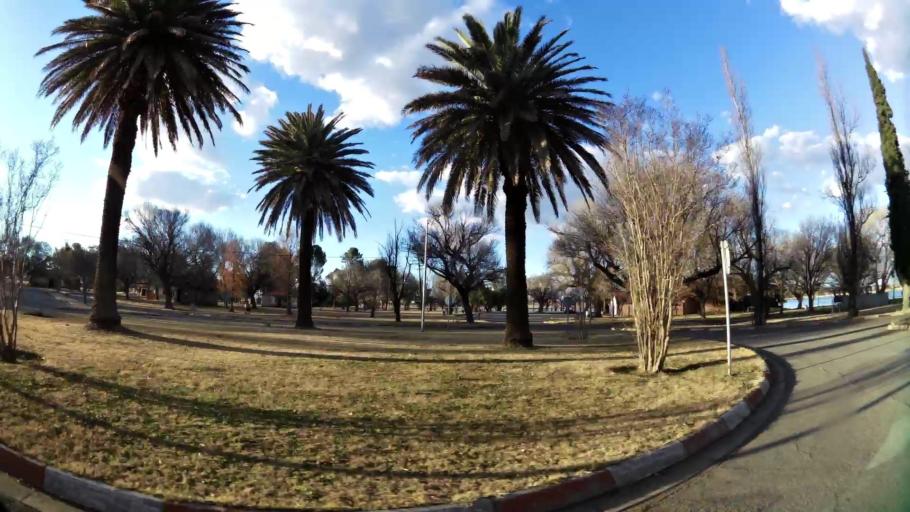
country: ZA
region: North-West
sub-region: Dr Kenneth Kaunda District Municipality
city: Potchefstroom
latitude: -26.6717
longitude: 27.0924
